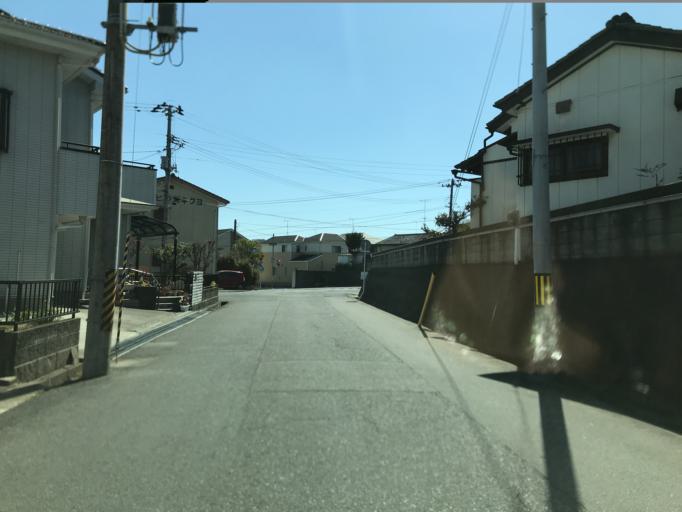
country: JP
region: Fukushima
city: Iwaki
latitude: 37.0477
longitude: 140.8577
